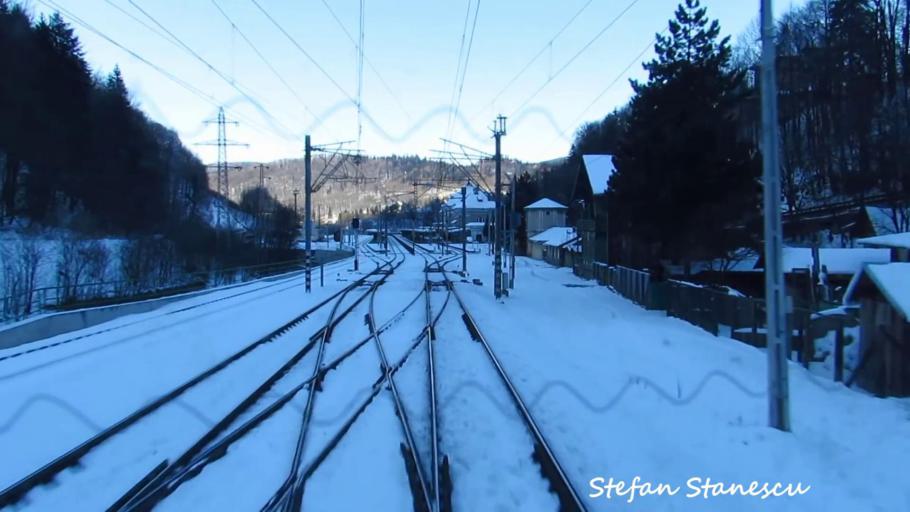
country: RO
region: Prahova
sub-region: Oras Sinaia
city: Sinaia
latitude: 45.3614
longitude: 25.5523
